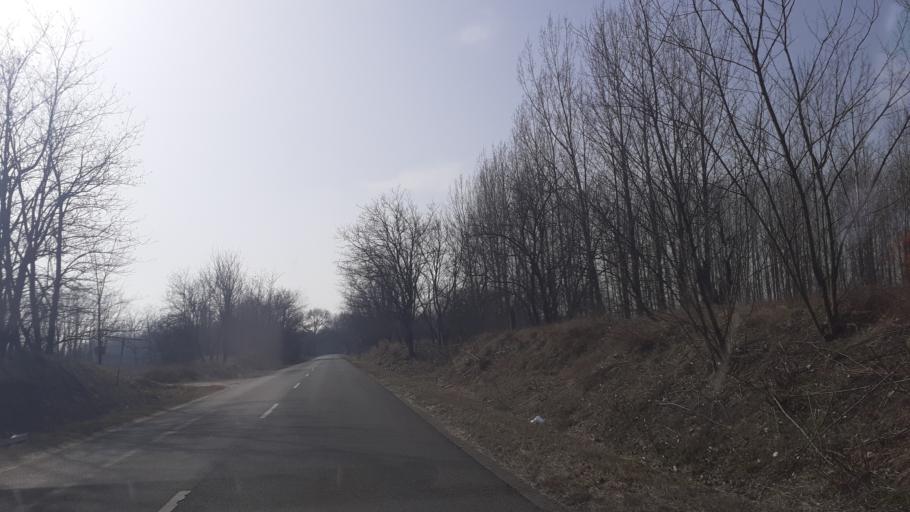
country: HU
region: Pest
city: Orkeny
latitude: 47.0925
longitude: 19.3828
